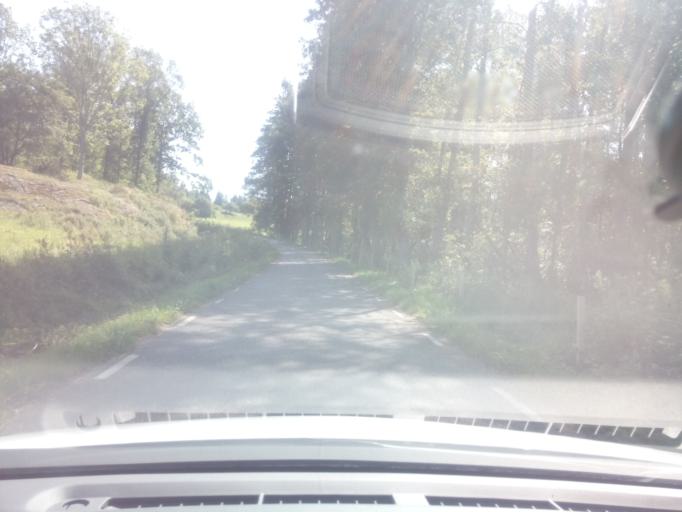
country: SE
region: Soedermanland
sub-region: Trosa Kommun
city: Trosa
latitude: 58.7977
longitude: 17.3732
